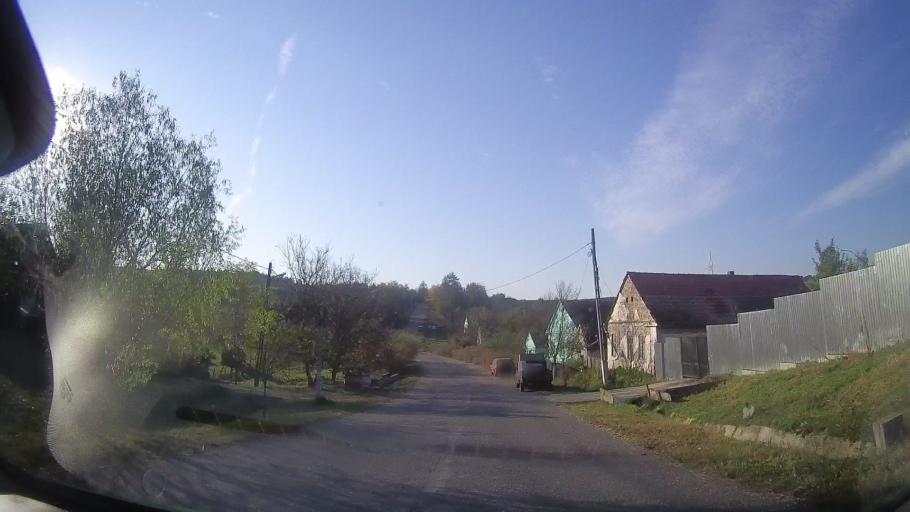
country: RO
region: Timis
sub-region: Comuna Bogda
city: Bogda
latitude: 45.9598
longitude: 21.6144
